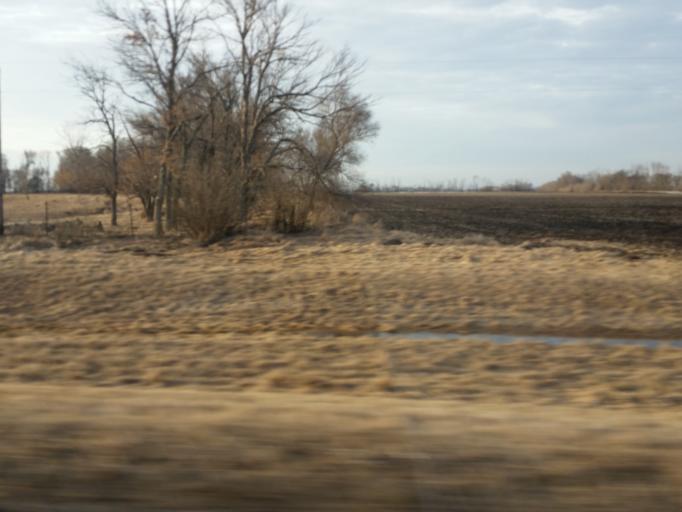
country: US
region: North Dakota
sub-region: Traill County
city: Mayville
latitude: 47.3530
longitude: -97.2954
